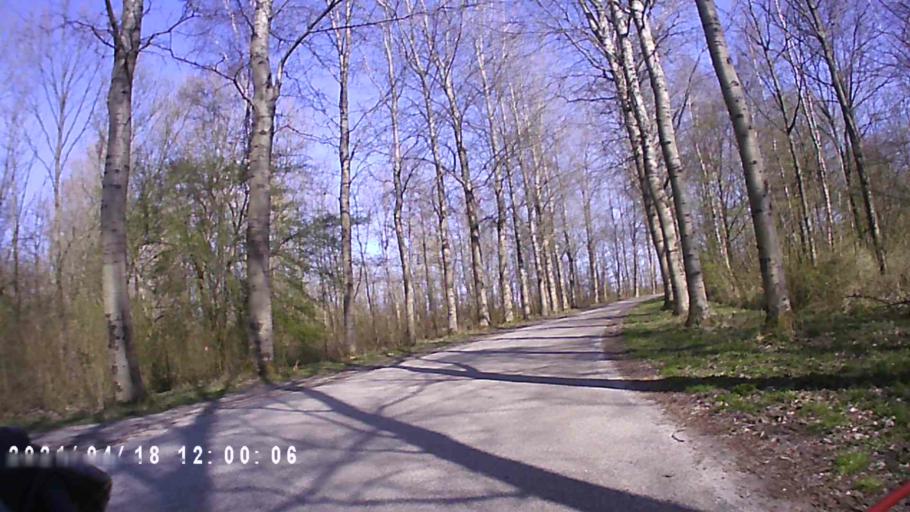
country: NL
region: Friesland
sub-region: Gemeente Kollumerland en Nieuwkruisland
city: Kollum
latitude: 53.3287
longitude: 6.1865
